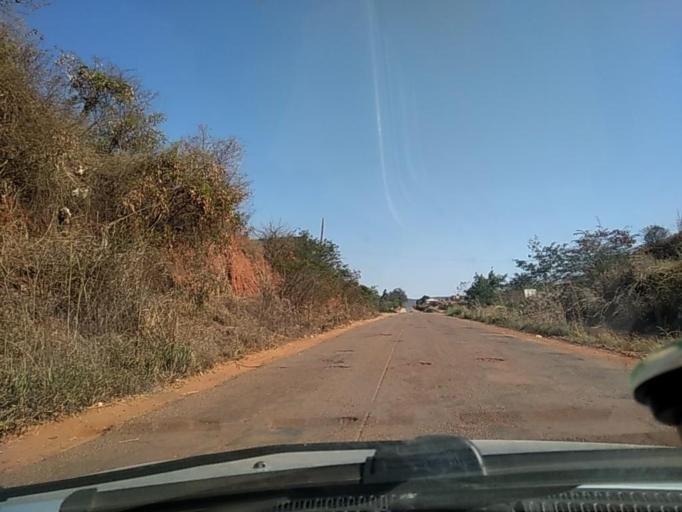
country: BR
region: Bahia
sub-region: Caetite
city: Caetite
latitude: -14.0470
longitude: -42.4853
